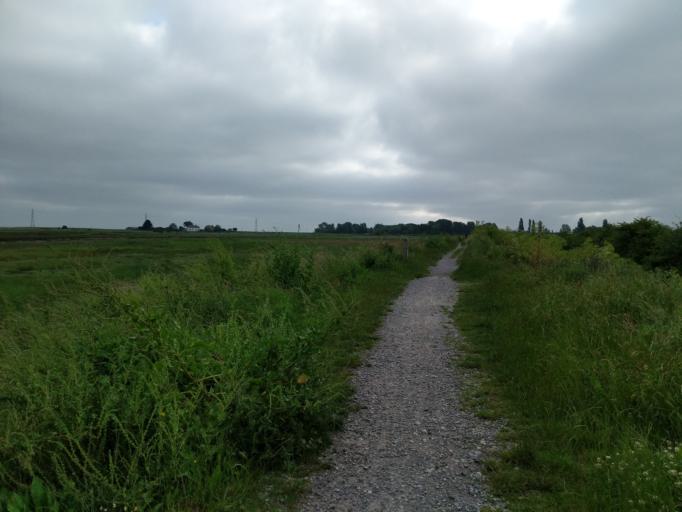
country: GB
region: England
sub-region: Kent
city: Faversham
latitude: 51.3246
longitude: 0.9097
